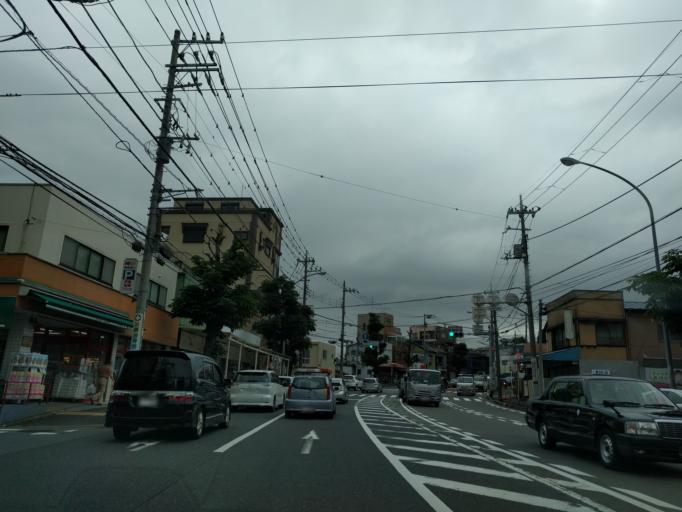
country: JP
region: Kanagawa
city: Yokohama
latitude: 35.4376
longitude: 139.5971
